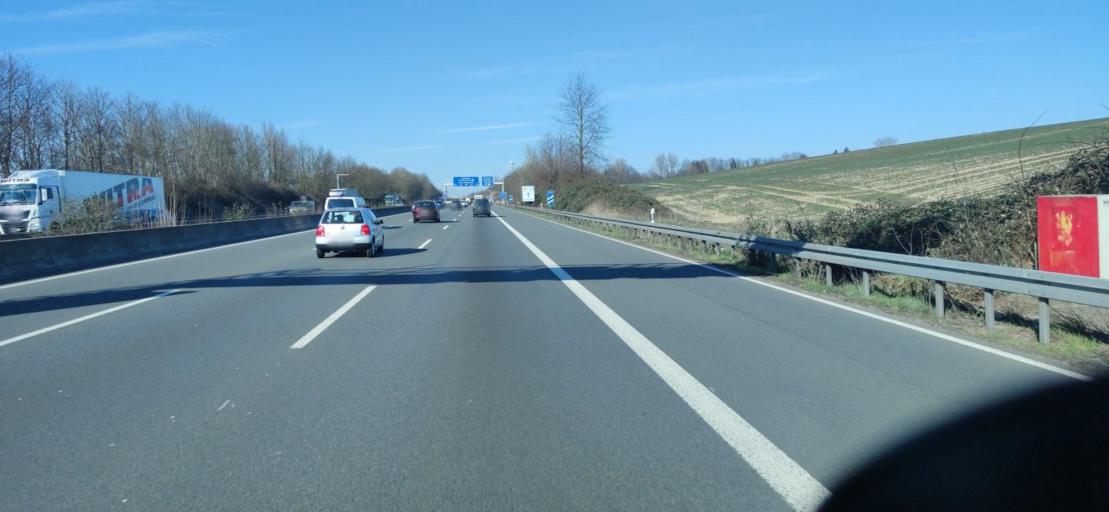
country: DE
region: North Rhine-Westphalia
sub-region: Regierungsbezirk Dusseldorf
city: Erkrath
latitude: 51.2522
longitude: 6.9111
